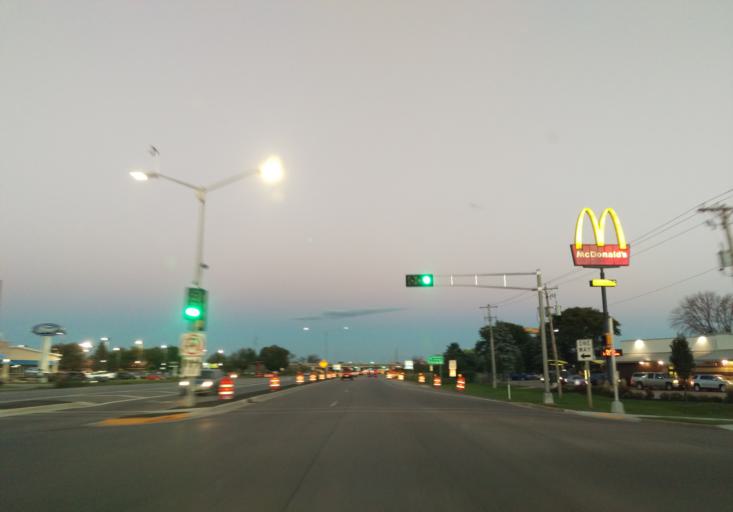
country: US
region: Wisconsin
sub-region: Rock County
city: Janesville
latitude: 42.7183
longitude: -88.9897
